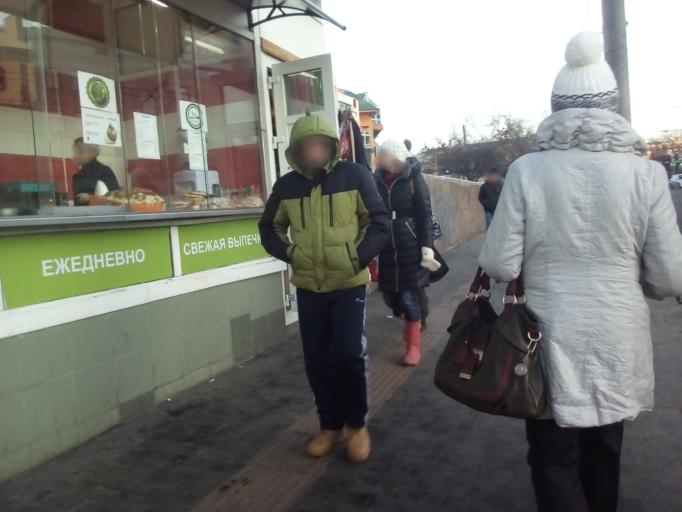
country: RU
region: Moskovskaya
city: Dorogomilovo
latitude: 55.7611
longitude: 37.5795
